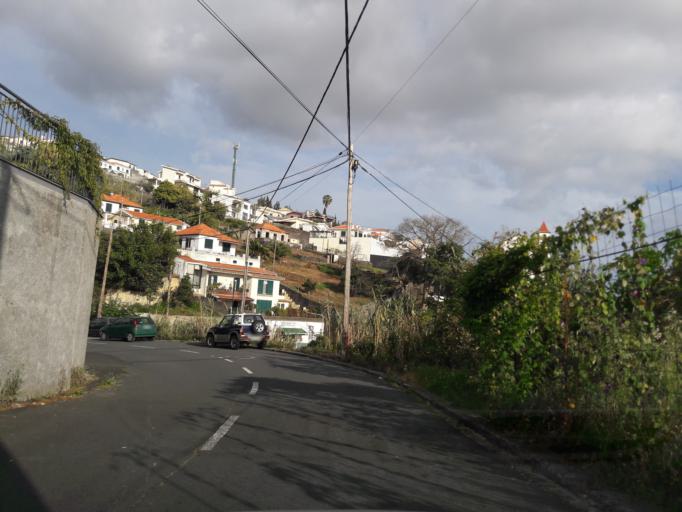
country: PT
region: Madeira
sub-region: Funchal
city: Nossa Senhora do Monte
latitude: 32.6585
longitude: -16.8909
